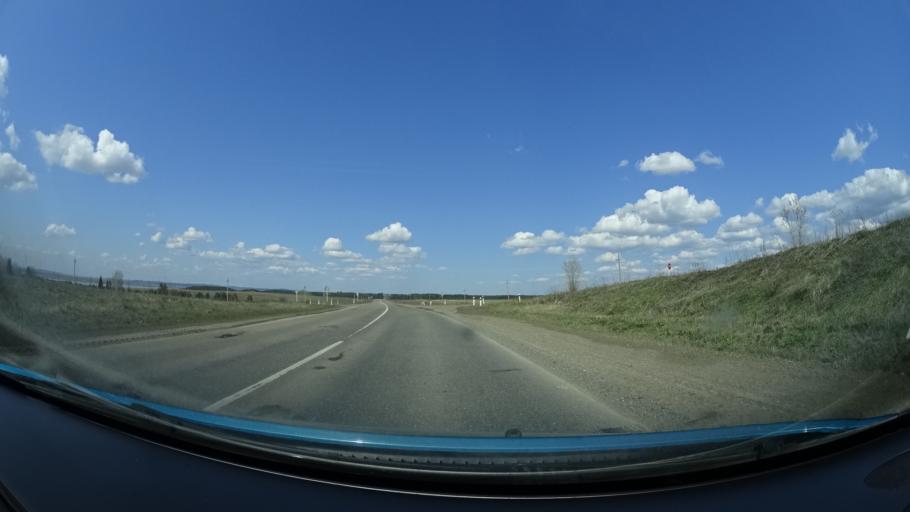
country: RU
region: Perm
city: Osa
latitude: 57.2400
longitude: 55.5964
